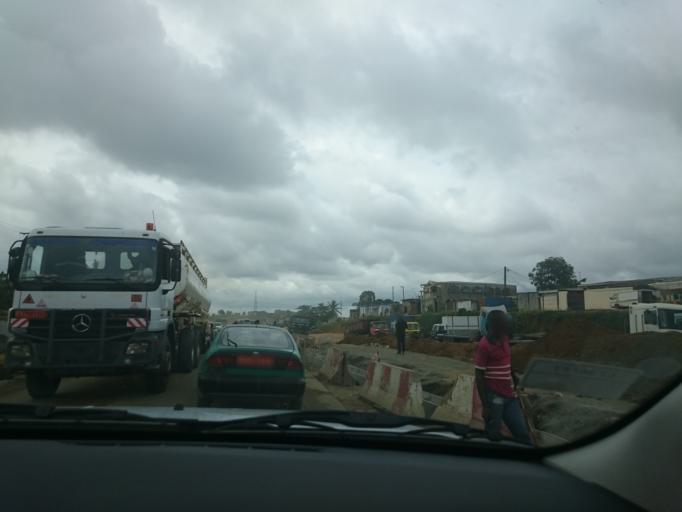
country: CM
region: Littoral
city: Douala
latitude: 3.9990
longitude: 9.7682
